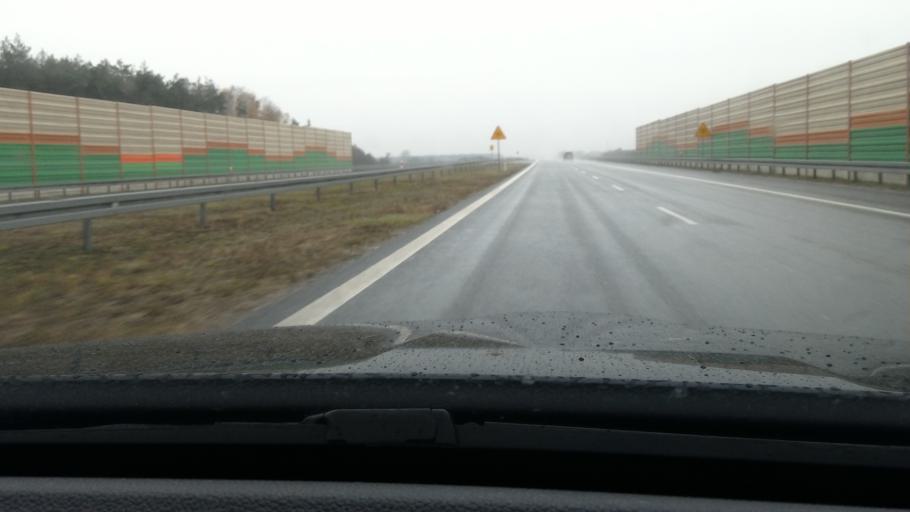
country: PL
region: Lodz Voivodeship
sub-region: Powiat skierniewicki
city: Bolimow
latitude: 52.0705
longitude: 20.1926
